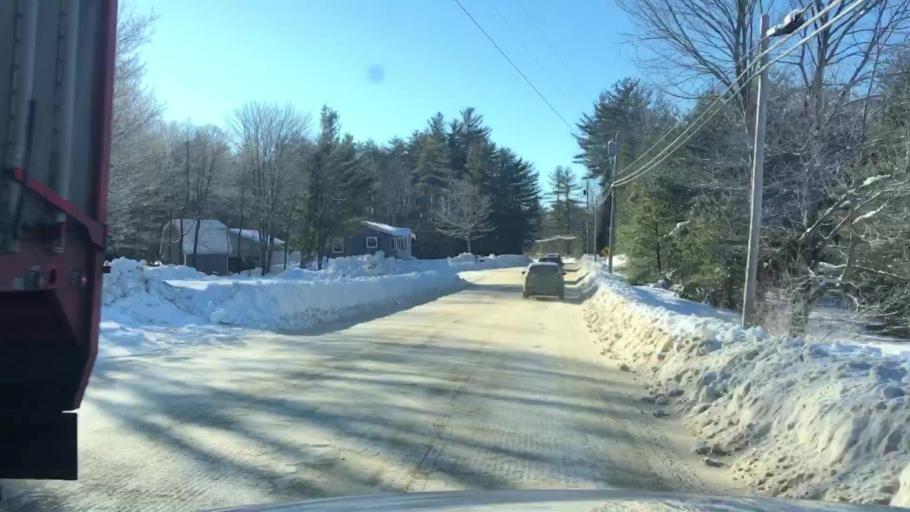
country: US
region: Maine
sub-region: Oxford County
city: West Paris
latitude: 44.3922
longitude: -70.6454
